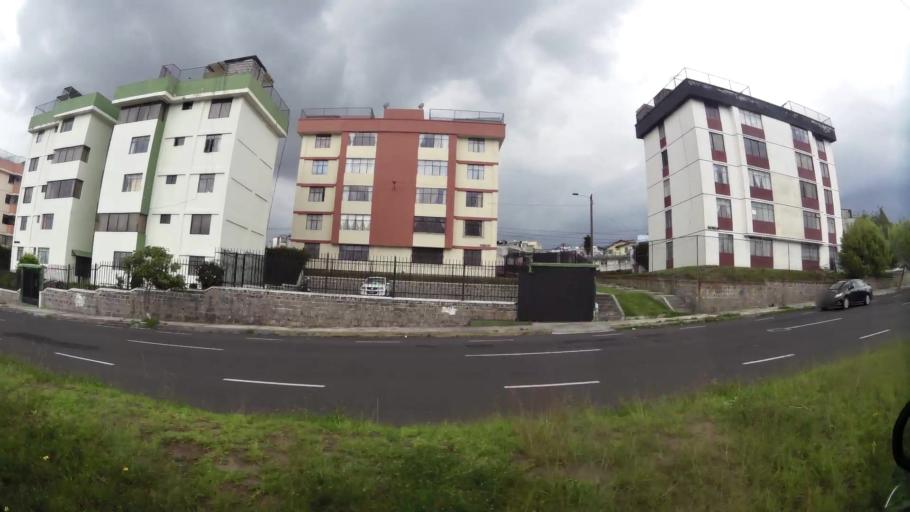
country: EC
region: Pichincha
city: Quito
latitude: -0.0846
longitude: -78.4721
